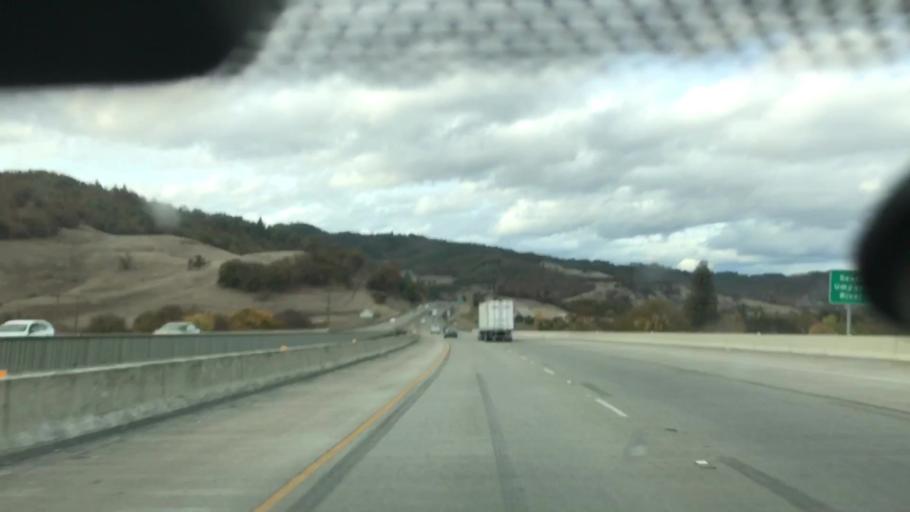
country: US
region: Oregon
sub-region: Douglas County
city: Green
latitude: 43.1684
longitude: -123.3665
